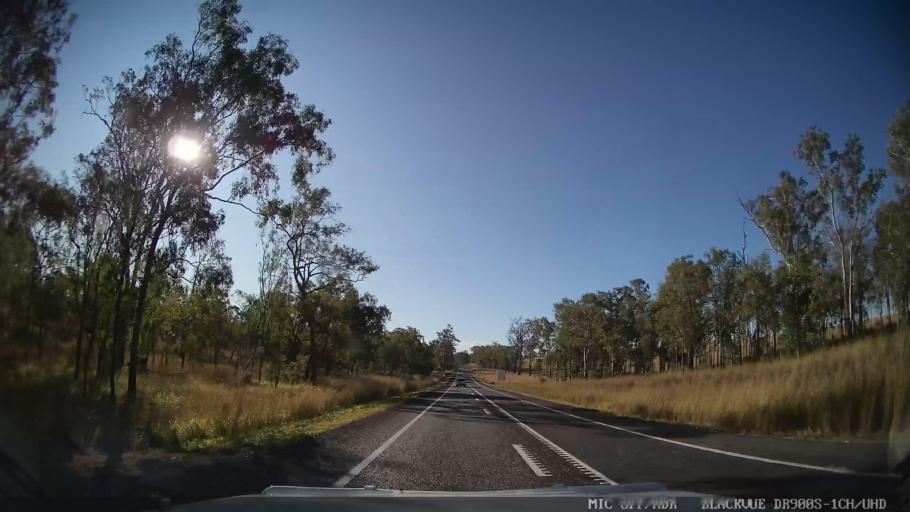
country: AU
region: Queensland
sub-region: Bundaberg
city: Sharon
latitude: -24.8353
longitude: 151.7098
